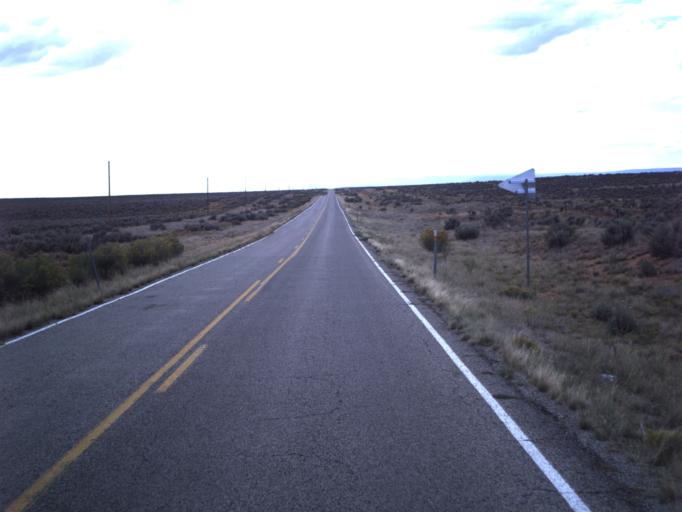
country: US
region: Utah
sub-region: San Juan County
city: Blanding
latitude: 37.4240
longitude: -109.3437
